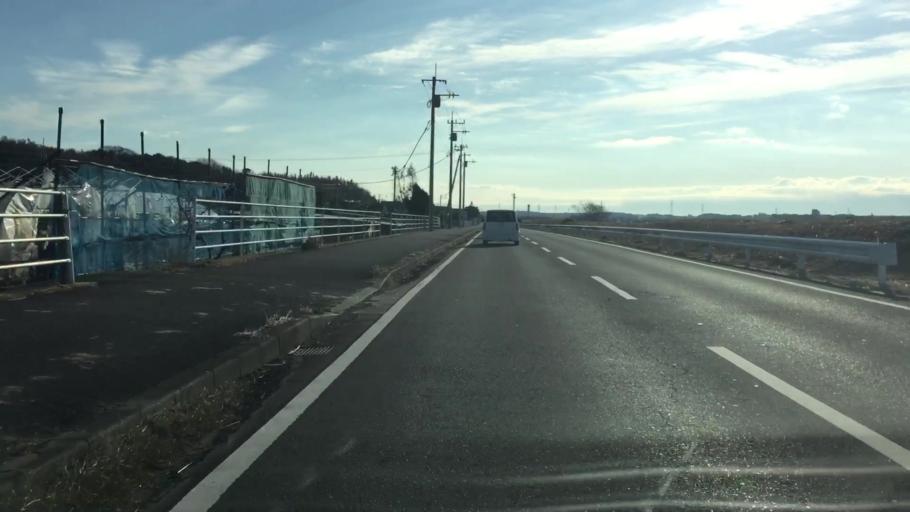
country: JP
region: Ibaraki
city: Toride
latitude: 35.8529
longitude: 140.1228
